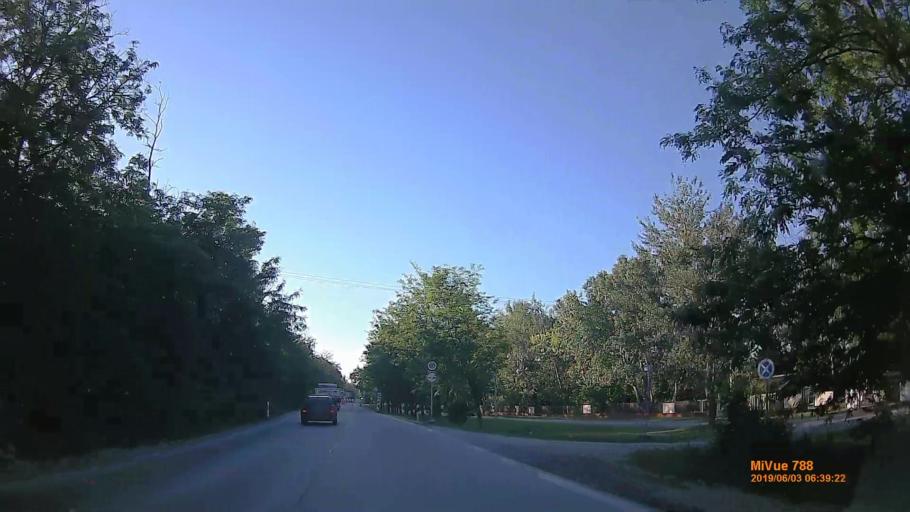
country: HU
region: Pest
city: Dunavarsany
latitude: 47.2876
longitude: 19.1000
